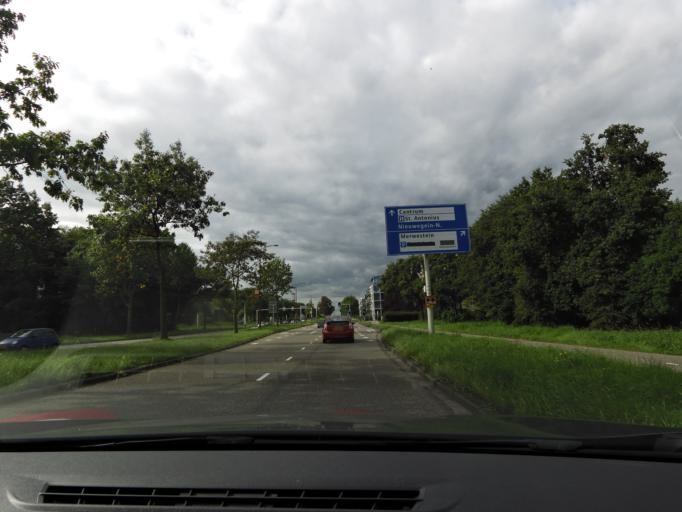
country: NL
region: Utrecht
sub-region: Gemeente Nieuwegein
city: Nieuwegein
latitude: 52.0248
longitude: 5.0913
